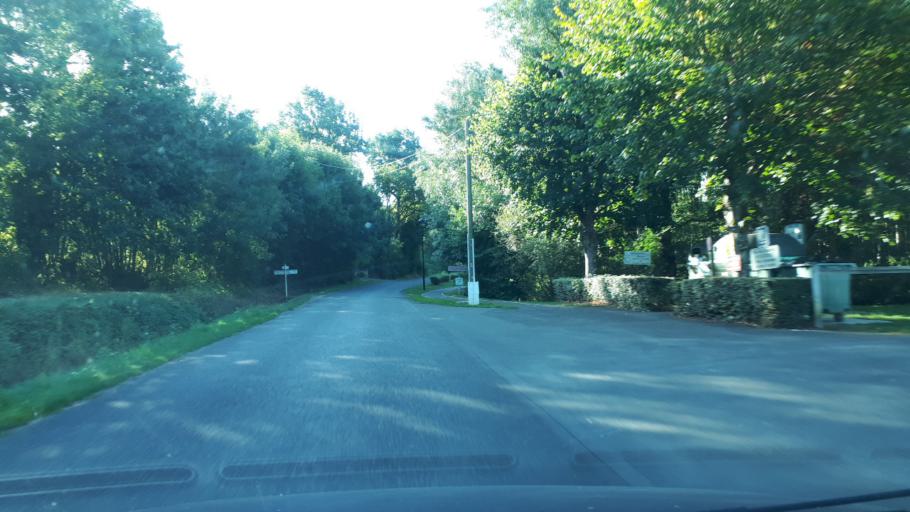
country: FR
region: Centre
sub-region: Departement d'Indre-et-Loire
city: Chateau-Renault
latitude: 47.6520
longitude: 0.9410
